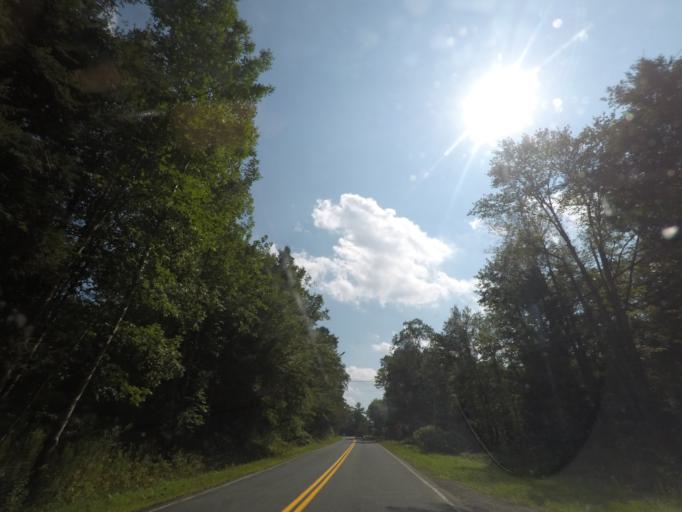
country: US
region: New York
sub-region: Rensselaer County
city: Poestenkill
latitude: 42.6998
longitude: -73.5151
